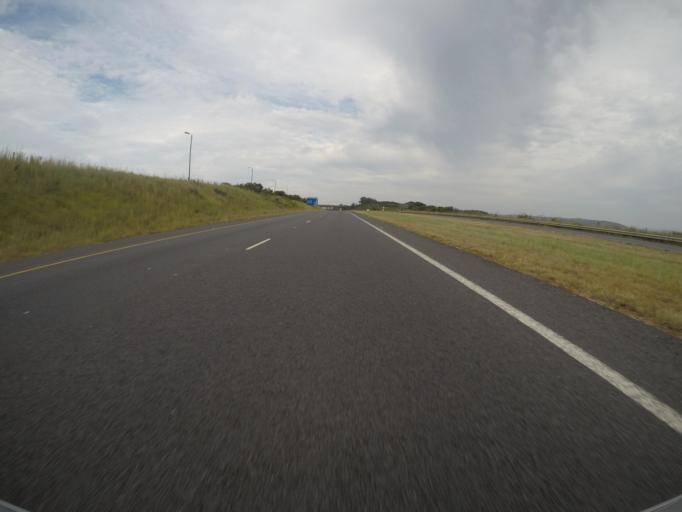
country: ZA
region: Eastern Cape
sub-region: Buffalo City Metropolitan Municipality
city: East London
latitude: -32.9700
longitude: 27.8694
